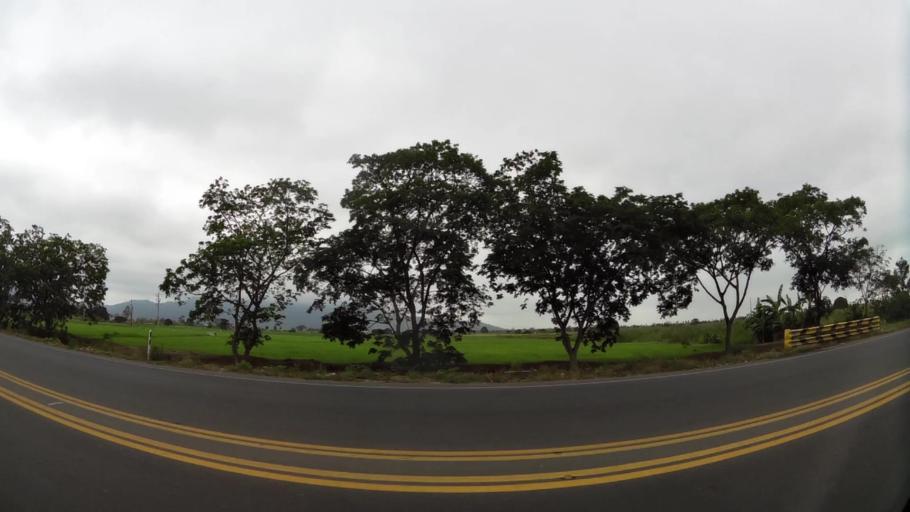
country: EC
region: Guayas
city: Naranjal
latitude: -2.4997
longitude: -79.5961
